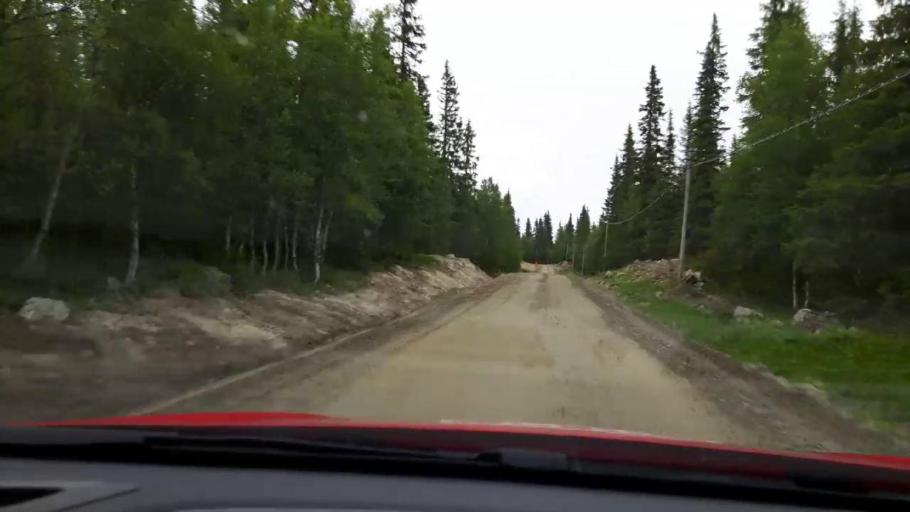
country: SE
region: Jaemtland
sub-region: Are Kommun
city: Are
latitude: 62.8202
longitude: 12.8136
